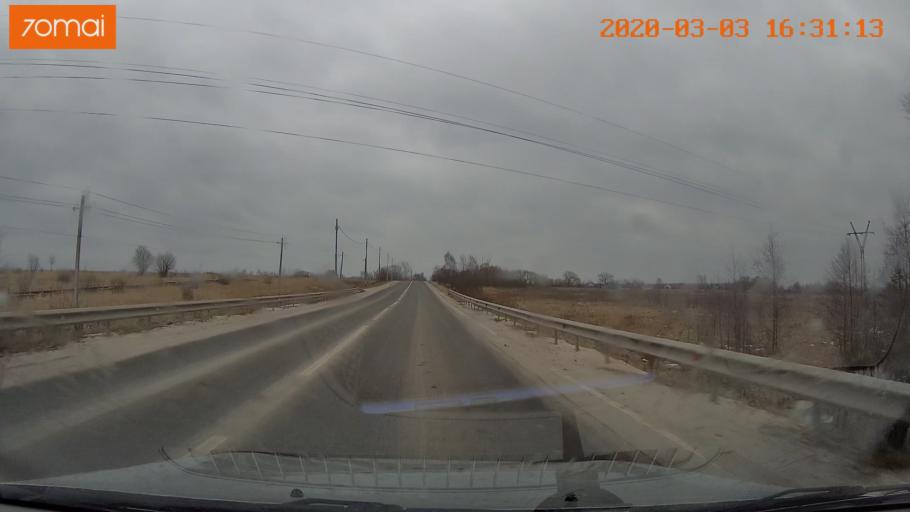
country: RU
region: Moskovskaya
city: Konobeyevo
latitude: 55.4272
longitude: 38.7219
